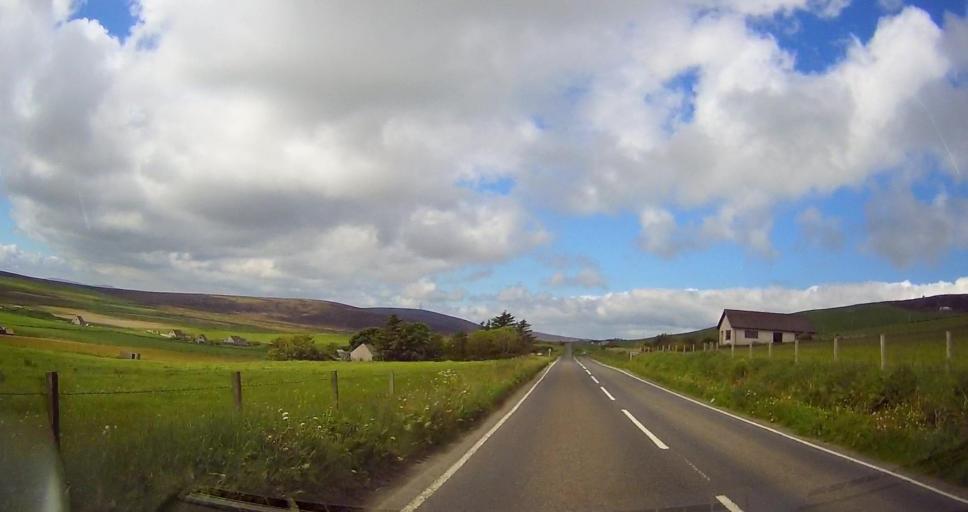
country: GB
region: Scotland
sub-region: Orkney Islands
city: Orkney
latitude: 58.9779
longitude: -3.0086
